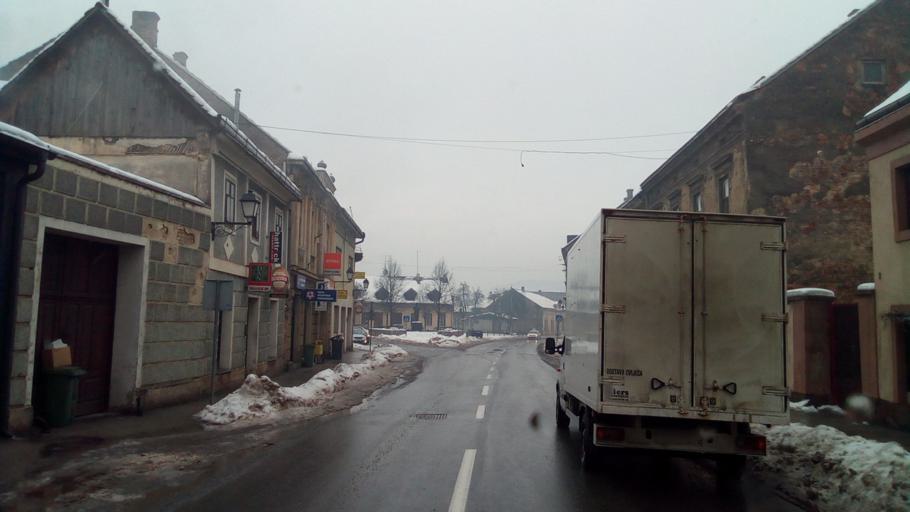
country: HR
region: Sisacko-Moslavacka
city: Petrinja
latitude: 45.4396
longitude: 16.2784
